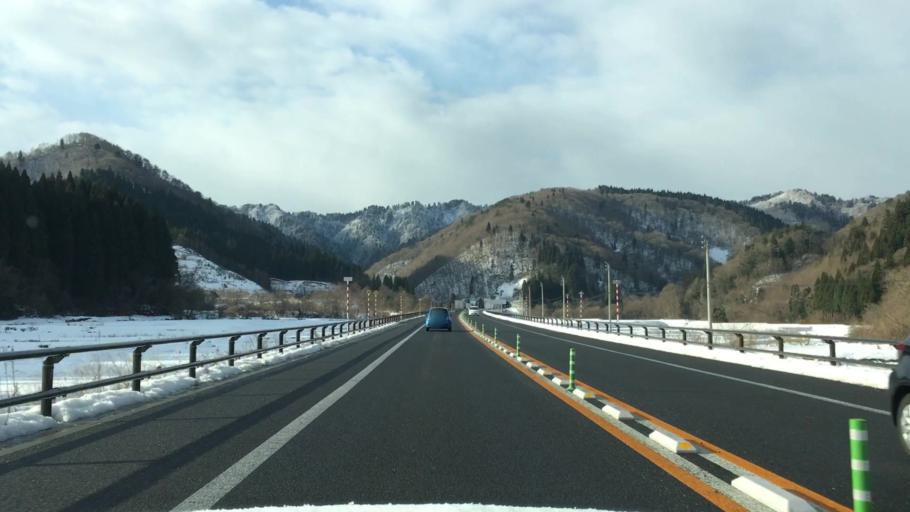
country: JP
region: Akita
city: Odate
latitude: 40.2340
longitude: 140.4965
